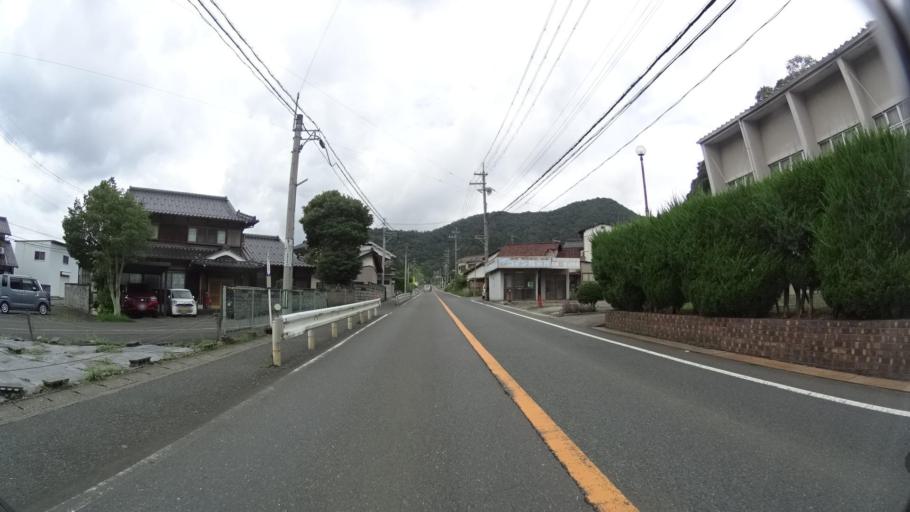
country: JP
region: Kyoto
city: Maizuru
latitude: 35.4962
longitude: 135.3920
